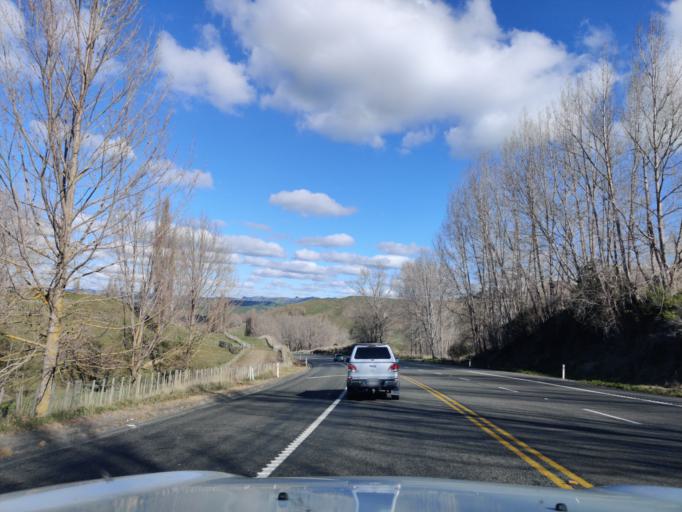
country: NZ
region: Manawatu-Wanganui
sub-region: Ruapehu District
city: Waiouru
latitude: -39.6029
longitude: 175.7612
